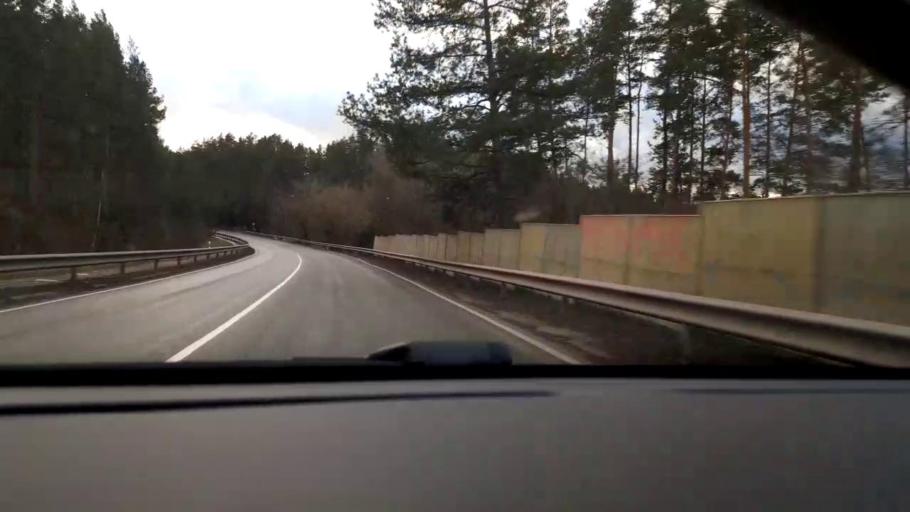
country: LT
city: Nemencine
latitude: 54.7884
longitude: 25.3847
